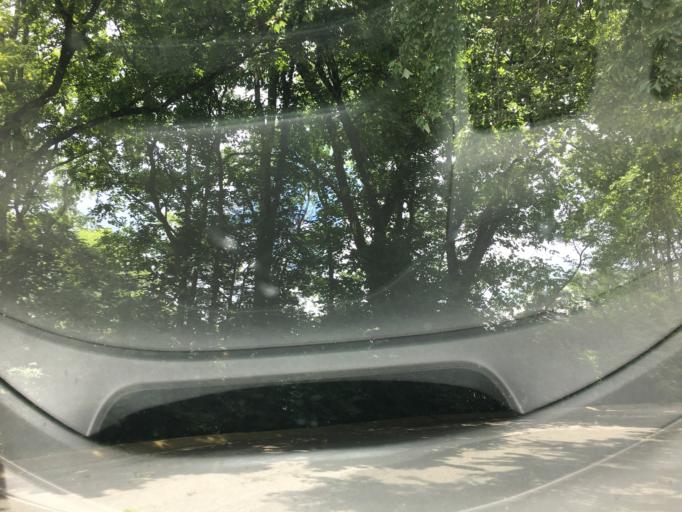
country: US
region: Tennessee
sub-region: Davidson County
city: Belle Meade
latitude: 36.0926
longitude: -86.8297
